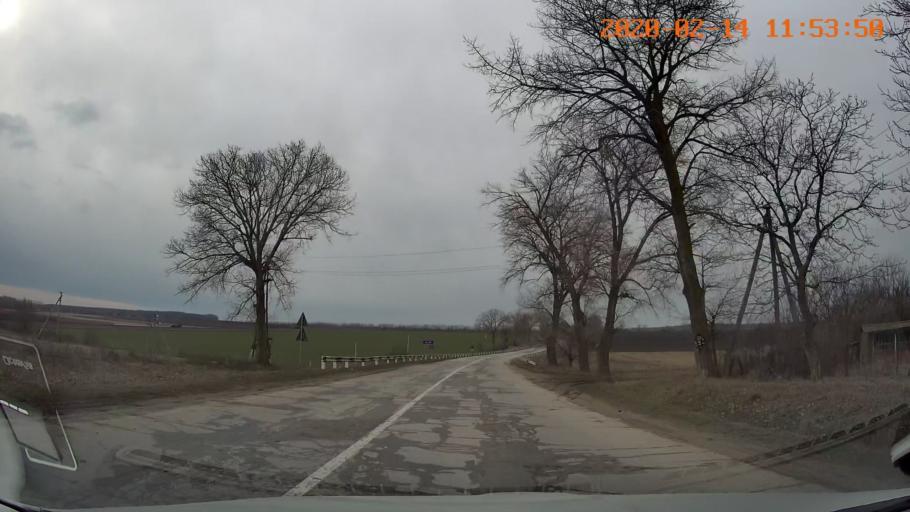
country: RO
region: Botosani
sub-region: Comuna Radauti-Prut
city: Miorcani
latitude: 48.2878
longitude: 26.8680
